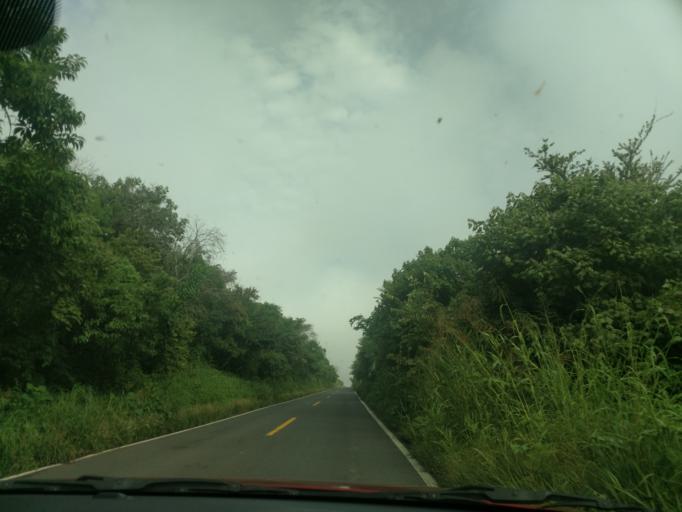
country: MX
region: Jalisco
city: Ameca
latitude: 20.5368
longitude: -104.1389
